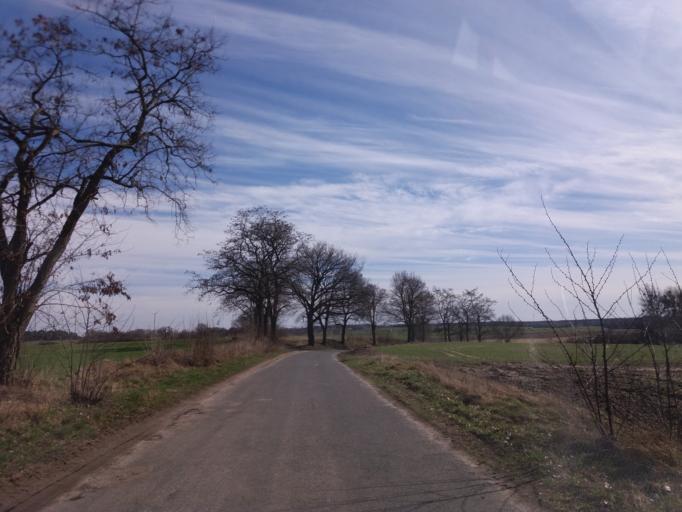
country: PL
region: West Pomeranian Voivodeship
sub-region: Powiat choszczenski
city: Choszczno
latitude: 53.1234
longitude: 15.3959
